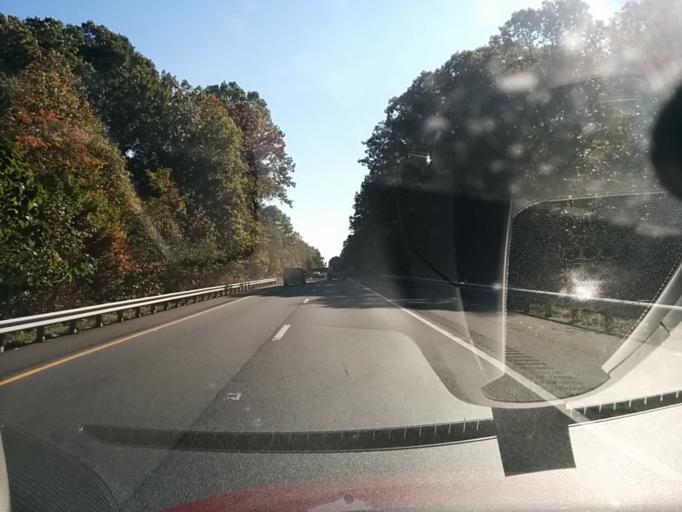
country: US
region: Virginia
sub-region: Albemarle County
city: Crozet
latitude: 38.0377
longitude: -78.7056
